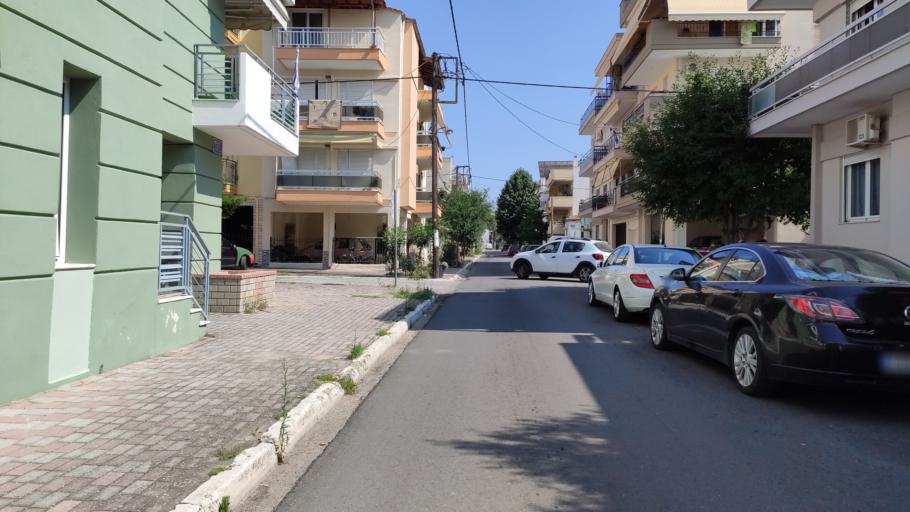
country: GR
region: East Macedonia and Thrace
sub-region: Nomos Rodopis
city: Komotini
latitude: 41.1164
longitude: 25.3910
